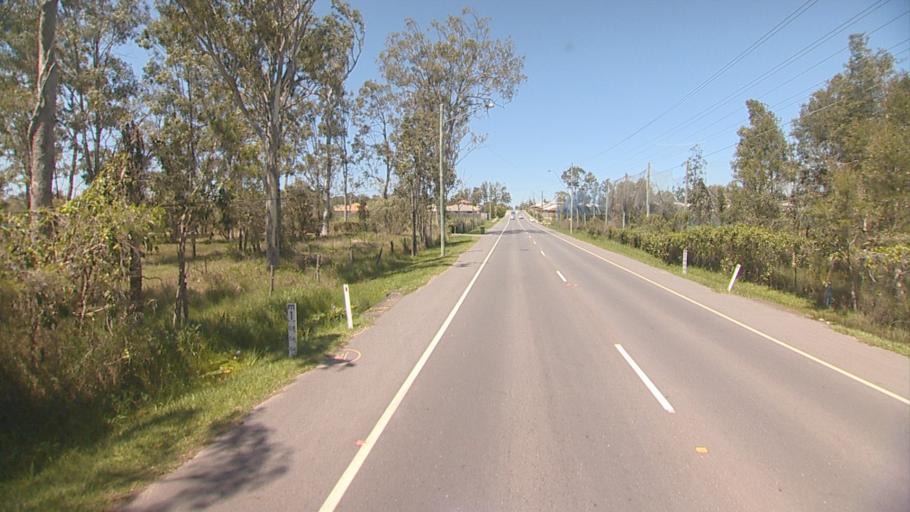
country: AU
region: Queensland
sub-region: Logan
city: Logan City
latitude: -27.6670
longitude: 153.0913
